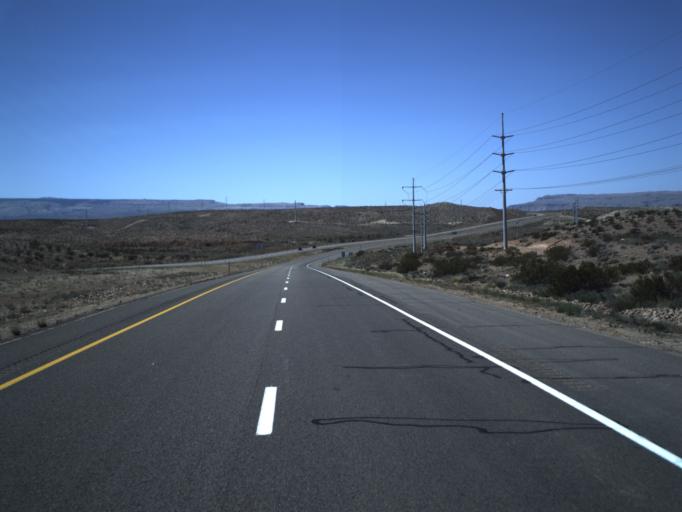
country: US
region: Utah
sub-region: Washington County
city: Saint George
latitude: 37.0062
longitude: -113.5223
